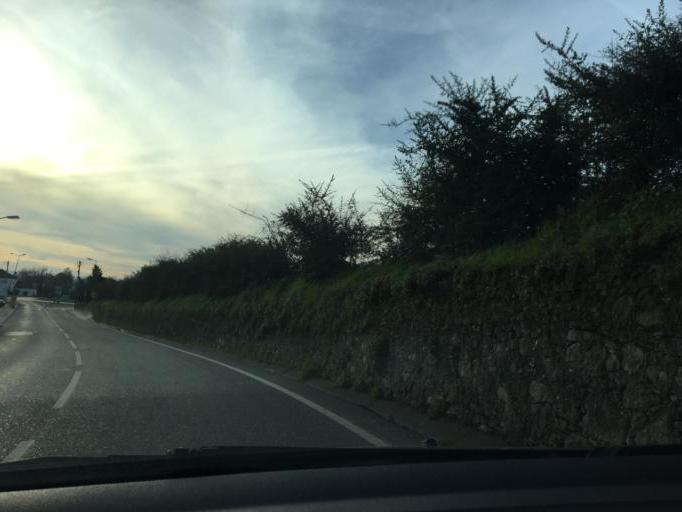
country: PT
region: Coimbra
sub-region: Montemor-O-Velho
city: Montemor-o-Velho
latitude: 40.1999
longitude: -8.6467
